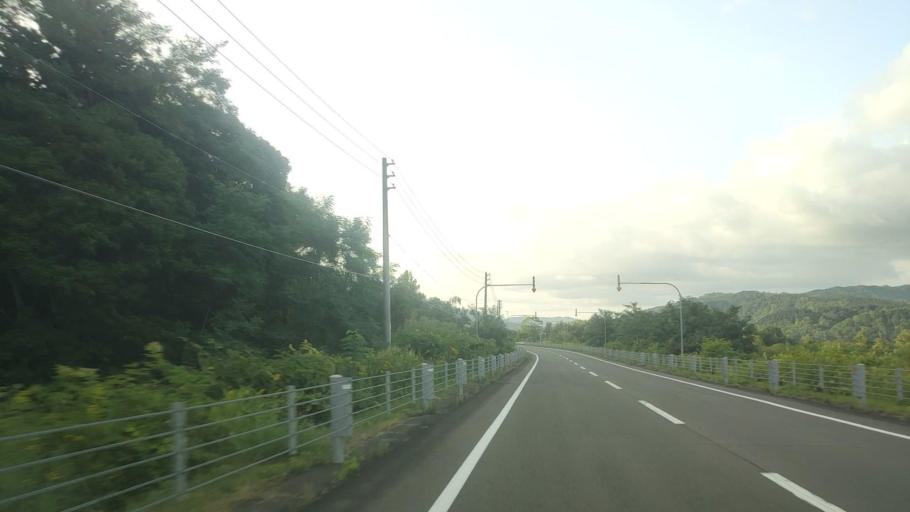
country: JP
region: Hokkaido
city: Bibai
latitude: 43.0765
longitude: 142.1020
